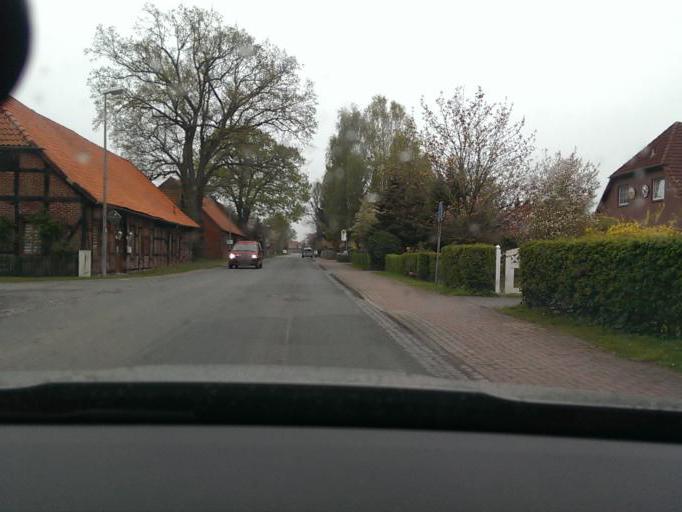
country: DE
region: Lower Saxony
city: Steimbke
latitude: 52.6497
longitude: 9.4901
